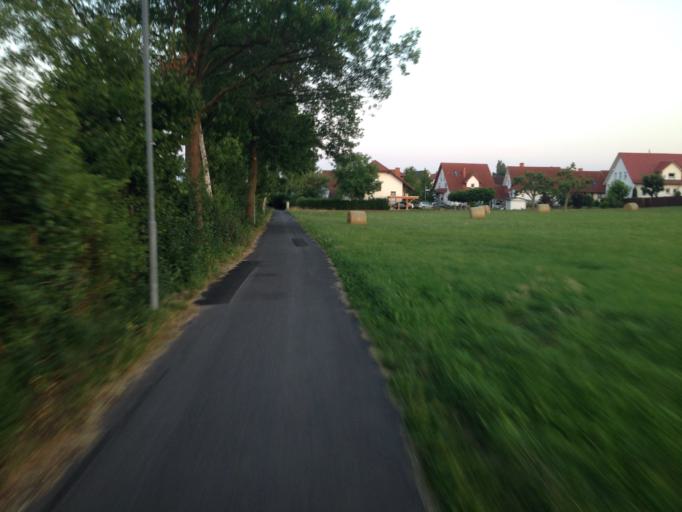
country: DE
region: Hesse
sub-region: Regierungsbezirk Giessen
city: Grossen Buseck
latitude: 50.5581
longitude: 8.7761
